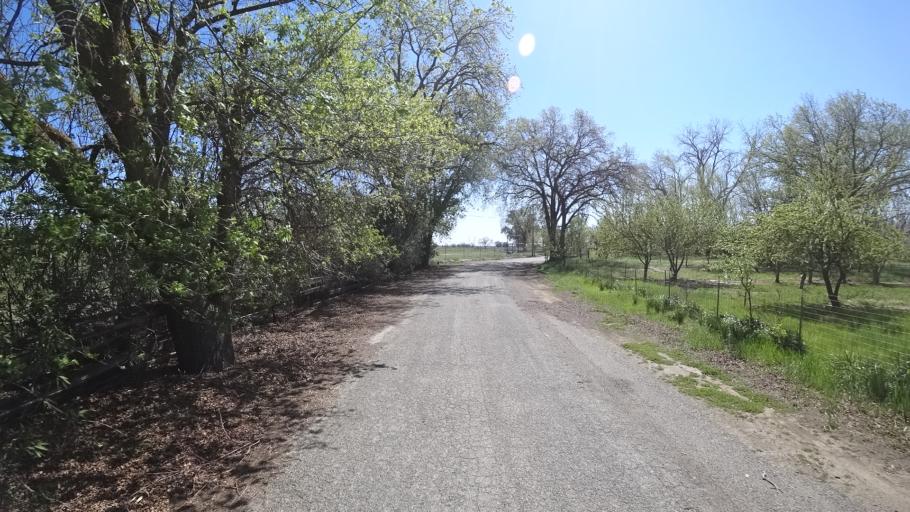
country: US
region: California
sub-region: Glenn County
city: Orland
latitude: 39.7833
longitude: -122.2716
